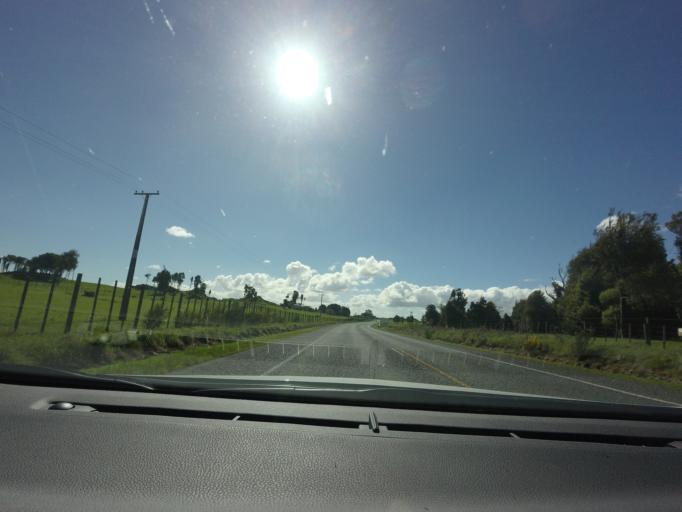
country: NZ
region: Bay of Plenty
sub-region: Rotorua District
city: Rotorua
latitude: -38.0536
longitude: 176.0825
